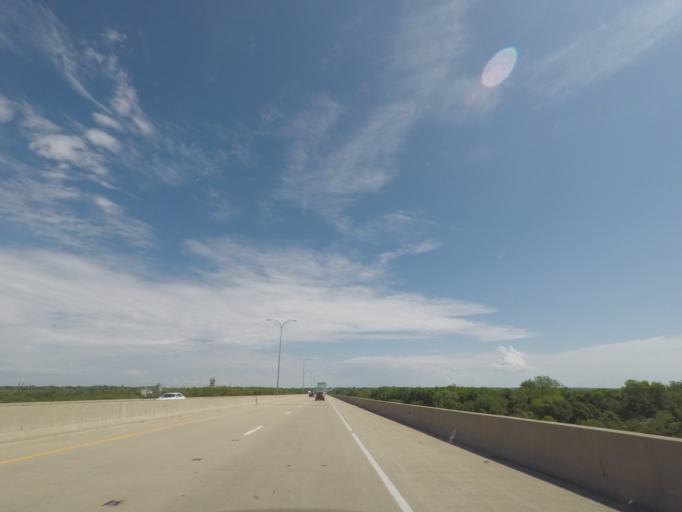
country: US
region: Illinois
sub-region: LaSalle County
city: La Salle
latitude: 41.3143
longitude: -89.0808
